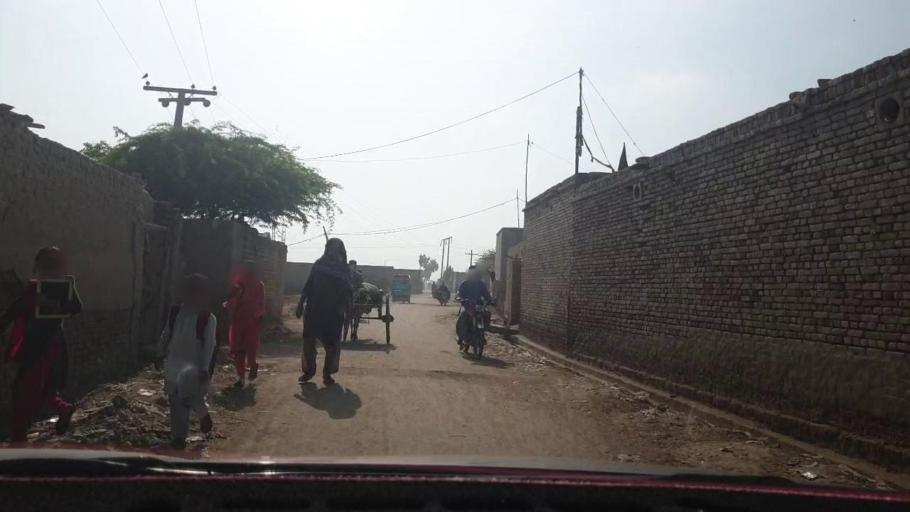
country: PK
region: Sindh
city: Nasirabad
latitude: 27.4429
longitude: 67.9455
